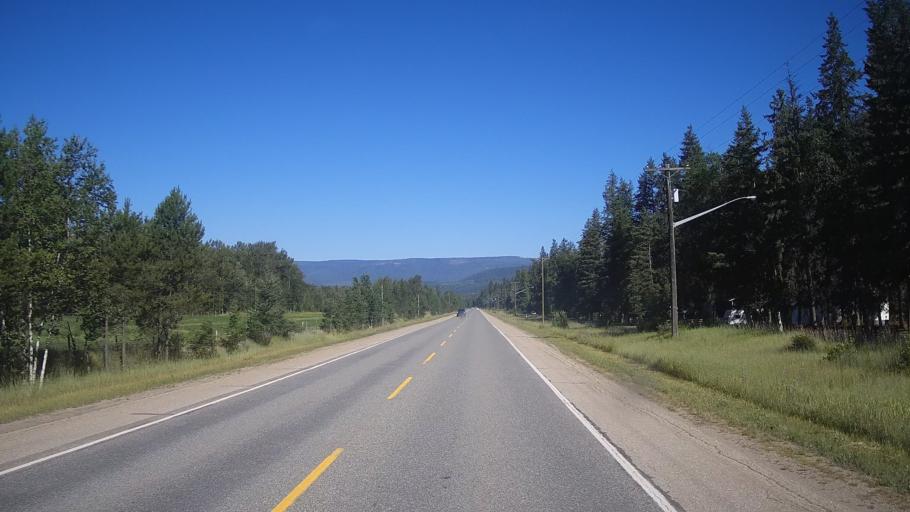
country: CA
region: British Columbia
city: Chase
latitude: 51.6232
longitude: -119.9443
